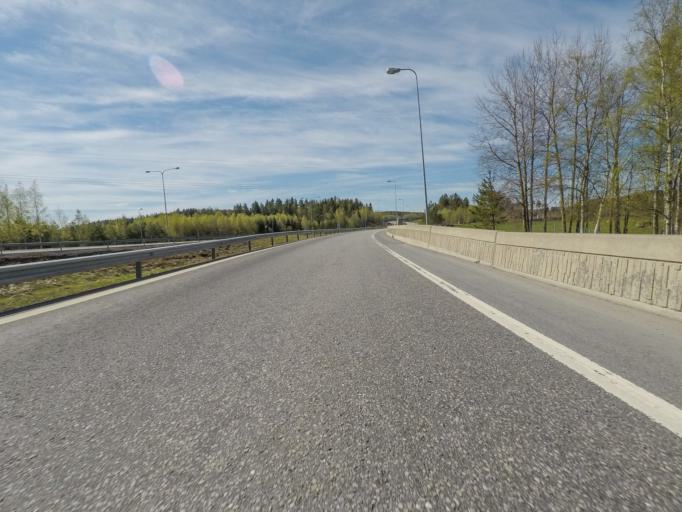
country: FI
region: Pirkanmaa
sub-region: Etelae-Pirkanmaa
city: Toijala
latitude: 61.2033
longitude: 23.8365
